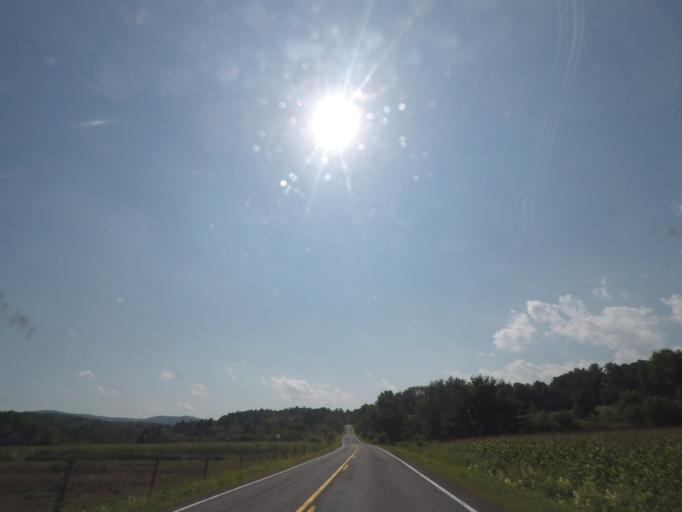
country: US
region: New York
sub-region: Rensselaer County
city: Hoosick Falls
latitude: 42.8425
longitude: -73.4634
